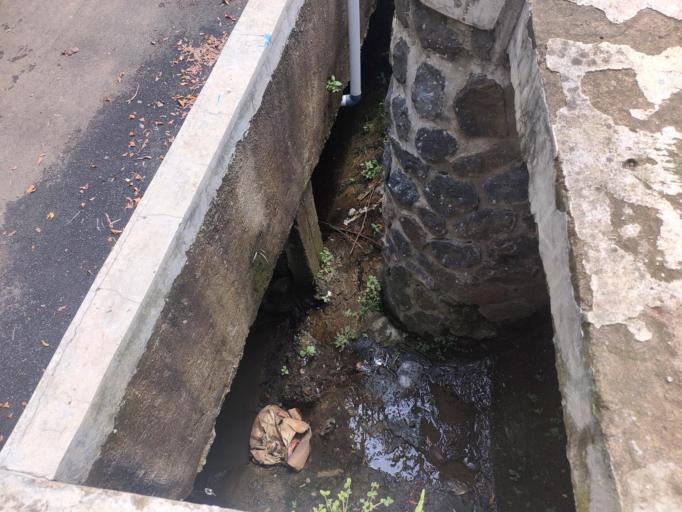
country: ID
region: West Java
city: Ciampea
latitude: -6.5197
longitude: 106.6860
